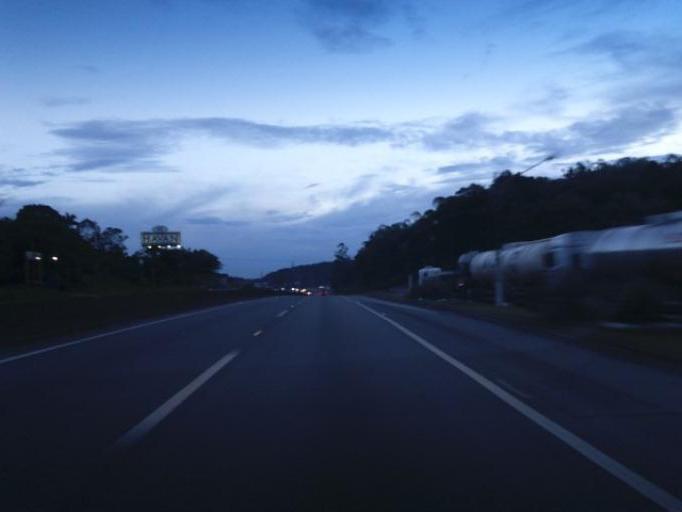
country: BR
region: Santa Catarina
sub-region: Joinville
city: Joinville
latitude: -26.3579
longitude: -48.8589
